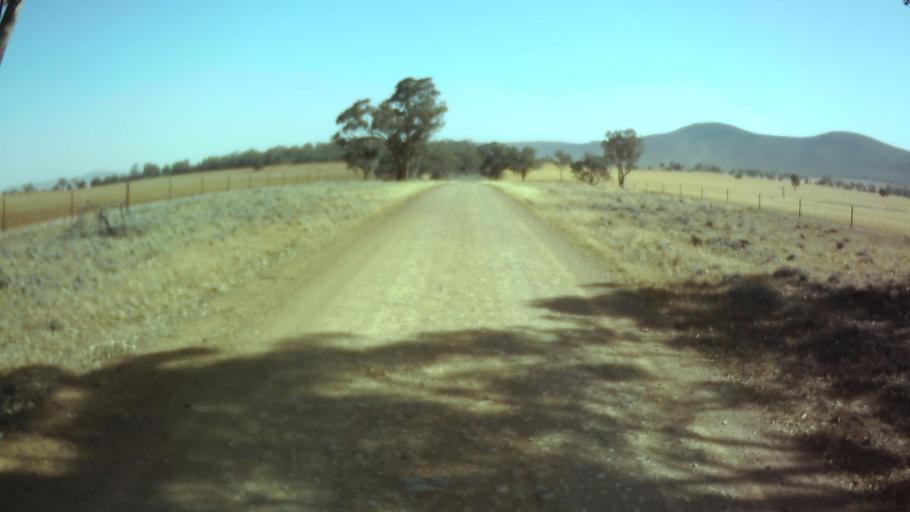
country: AU
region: New South Wales
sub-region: Weddin
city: Grenfell
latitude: -33.8521
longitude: 148.0162
